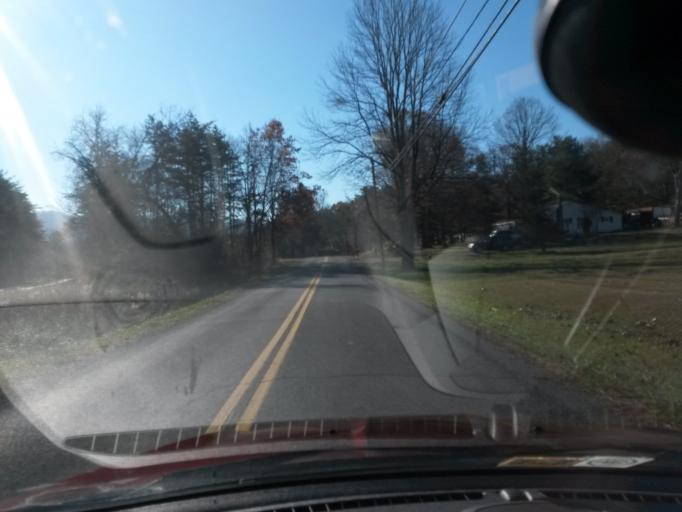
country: US
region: Virginia
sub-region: Alleghany County
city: Clifton Forge
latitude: 37.8101
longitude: -79.7434
